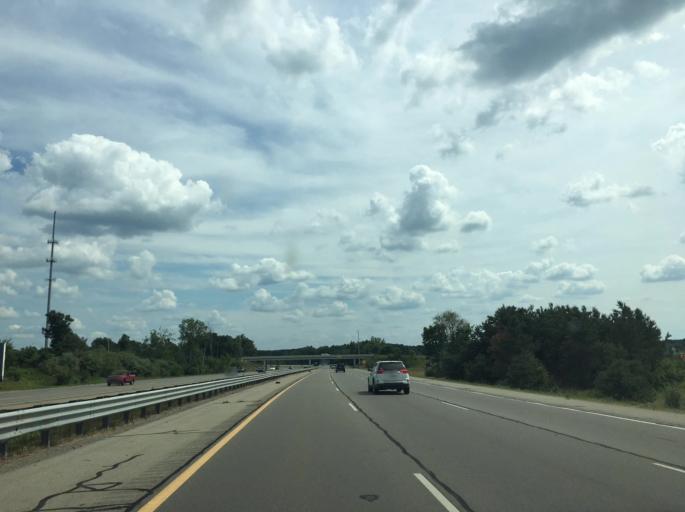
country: US
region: Michigan
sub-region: Oakland County
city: Holly
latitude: 42.8186
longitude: -83.5700
